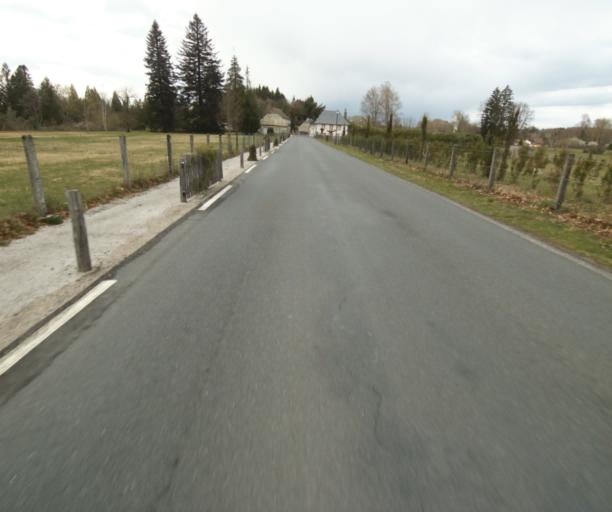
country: FR
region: Limousin
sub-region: Departement de la Correze
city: Saint-Privat
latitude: 45.2180
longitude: 2.0041
